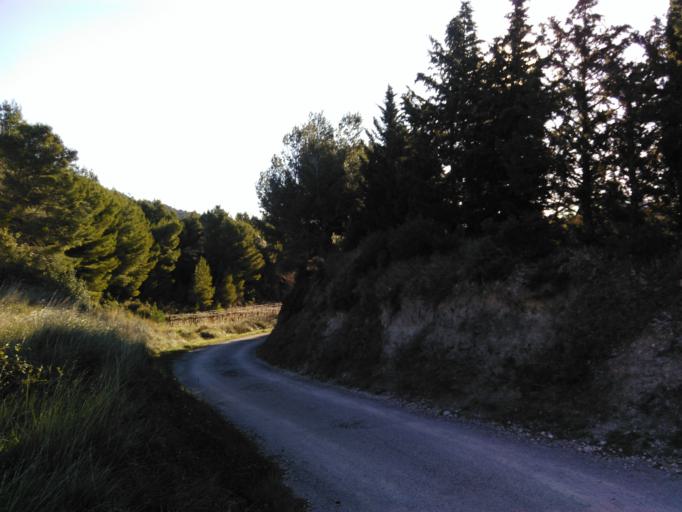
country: FR
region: Provence-Alpes-Cote d'Azur
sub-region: Departement du Vaucluse
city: Beaumes-de-Venise
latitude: 44.1339
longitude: 5.0562
